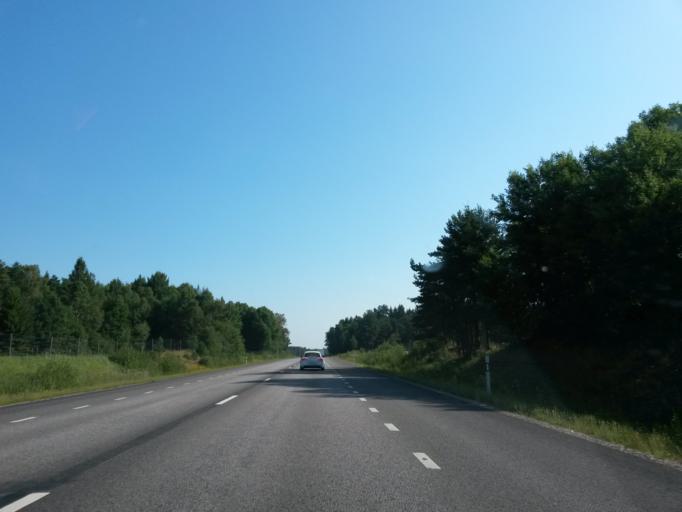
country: SE
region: Vaestra Goetaland
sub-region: Vara Kommun
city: Vara
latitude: 58.1599
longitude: 12.8788
